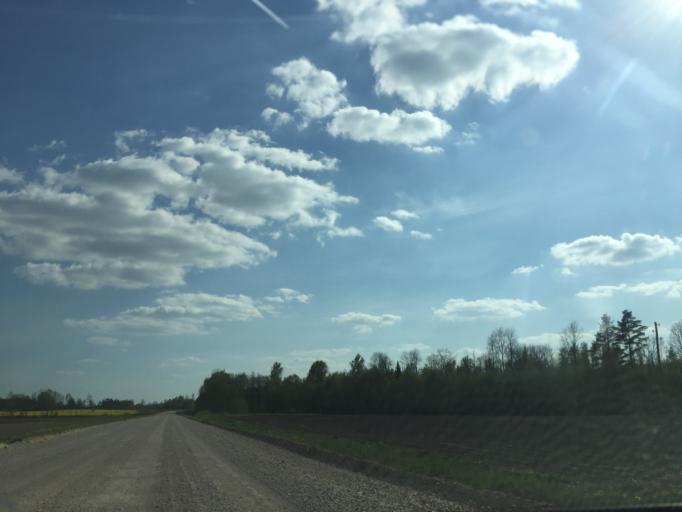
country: LV
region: Vecumnieki
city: Vecumnieki
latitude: 56.5356
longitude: 24.4204
